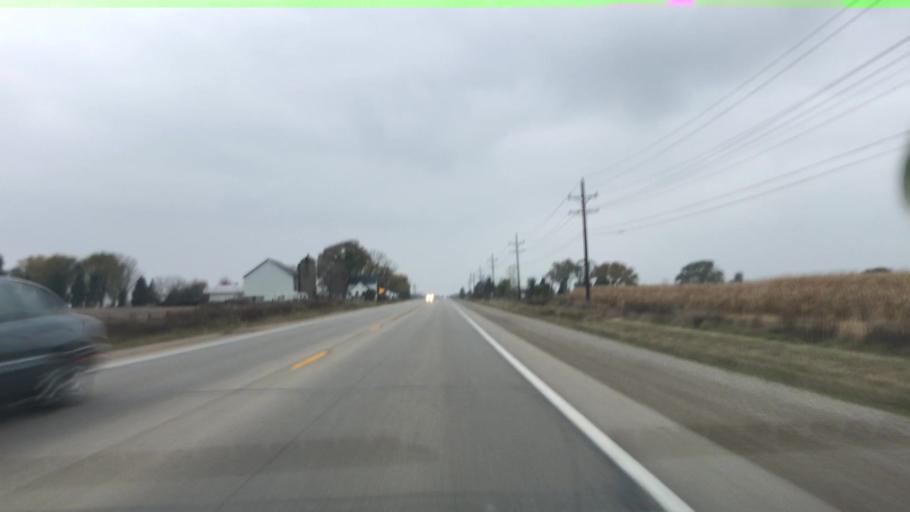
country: US
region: Wisconsin
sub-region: Outagamie County
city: Seymour
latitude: 44.5004
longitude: -88.3043
